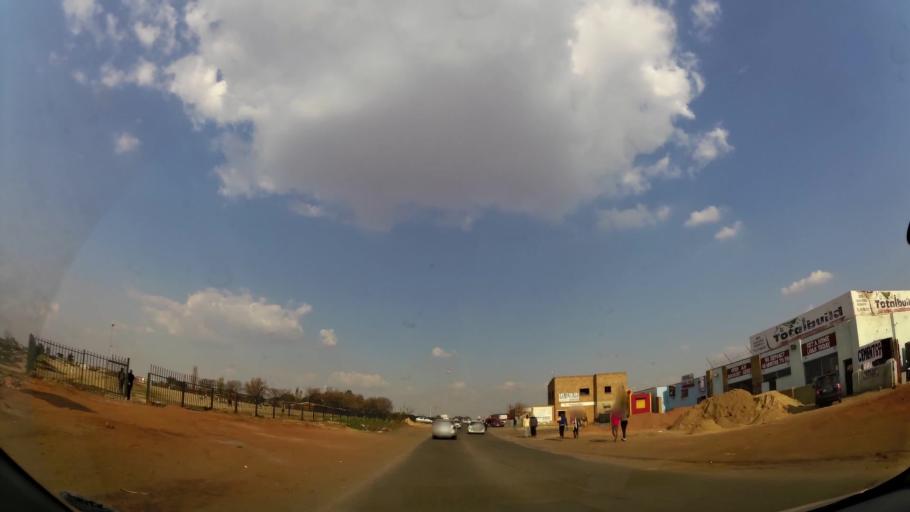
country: ZA
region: Gauteng
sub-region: Ekurhuleni Metropolitan Municipality
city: Germiston
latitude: -26.3467
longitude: 28.1870
